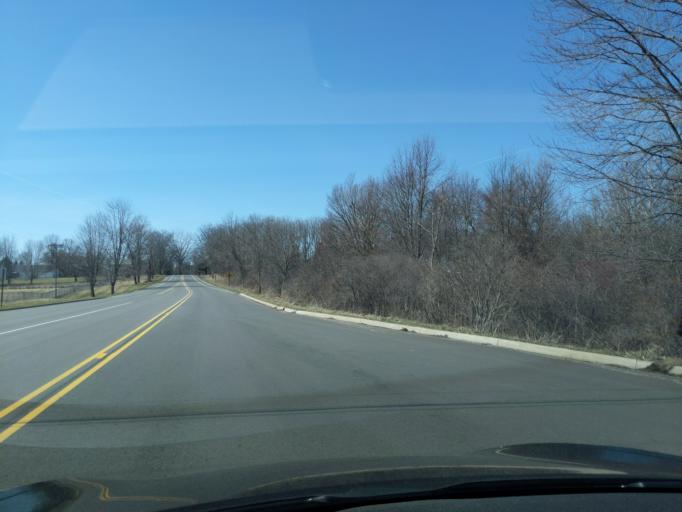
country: US
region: Michigan
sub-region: Eaton County
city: Grand Ledge
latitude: 42.7266
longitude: -84.7014
